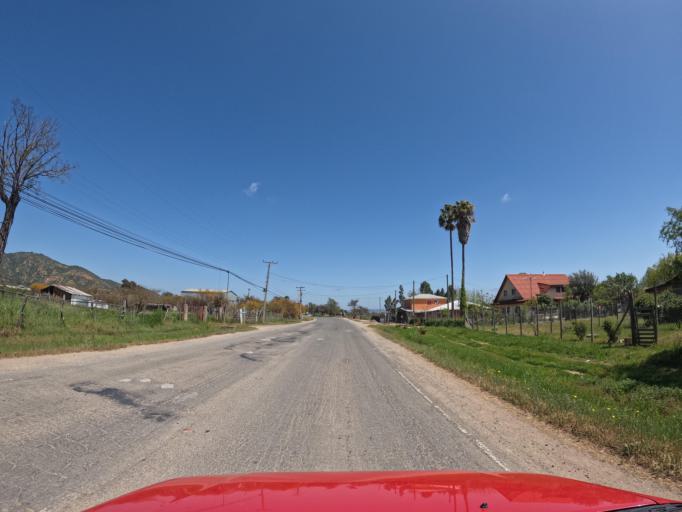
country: CL
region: O'Higgins
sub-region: Provincia de Colchagua
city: Santa Cruz
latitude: -34.7288
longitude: -71.6668
